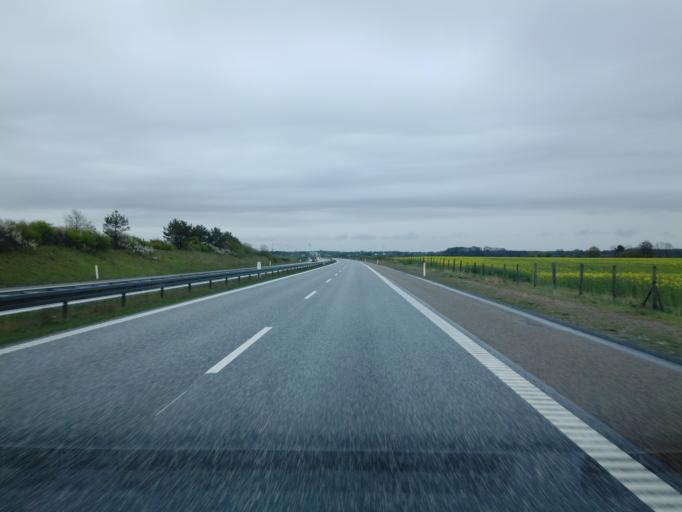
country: DK
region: North Denmark
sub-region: Frederikshavn Kommune
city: Saeby
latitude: 57.2897
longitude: 10.4135
